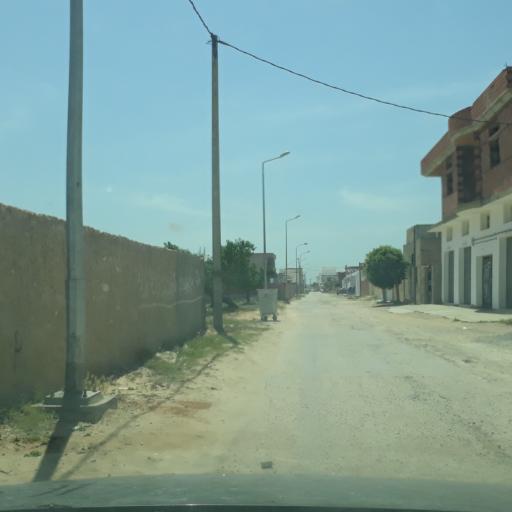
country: TN
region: Safaqis
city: Al Qarmadah
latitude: 34.8261
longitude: 10.7786
